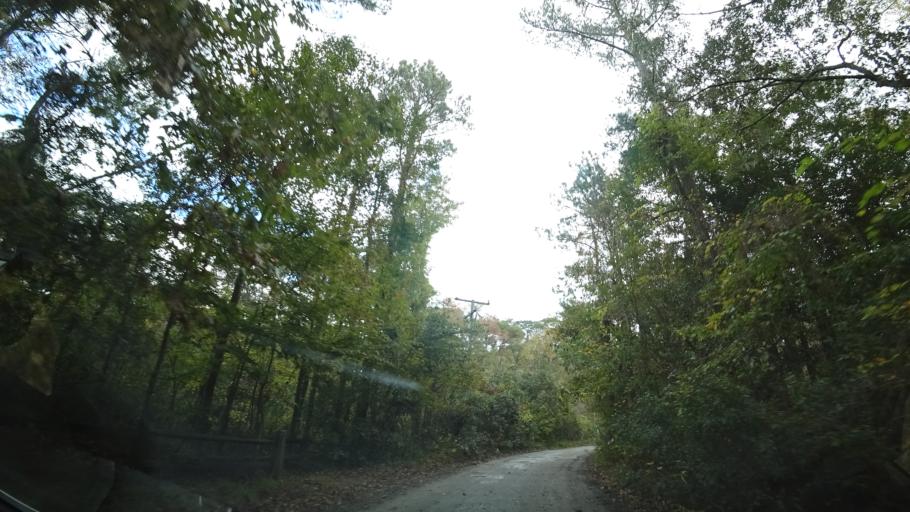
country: US
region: North Carolina
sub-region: Dare County
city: Kill Devil Hills
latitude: 35.9903
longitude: -75.6650
